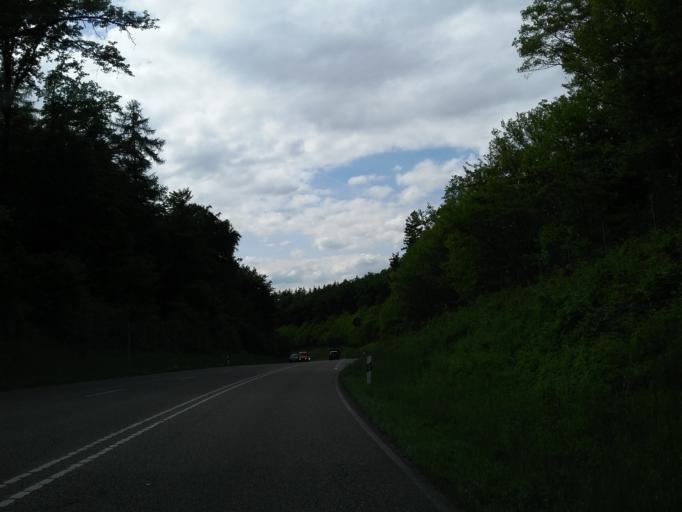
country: DE
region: Baden-Wuerttemberg
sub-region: Regierungsbezirk Stuttgart
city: Flein
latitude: 49.1077
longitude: 9.2433
